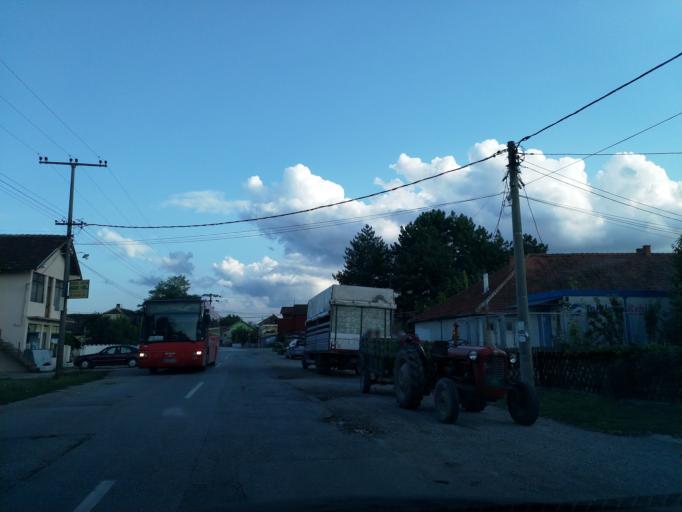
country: RS
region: Central Serbia
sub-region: Rasinski Okrug
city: Cicevac
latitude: 43.7650
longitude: 21.4292
